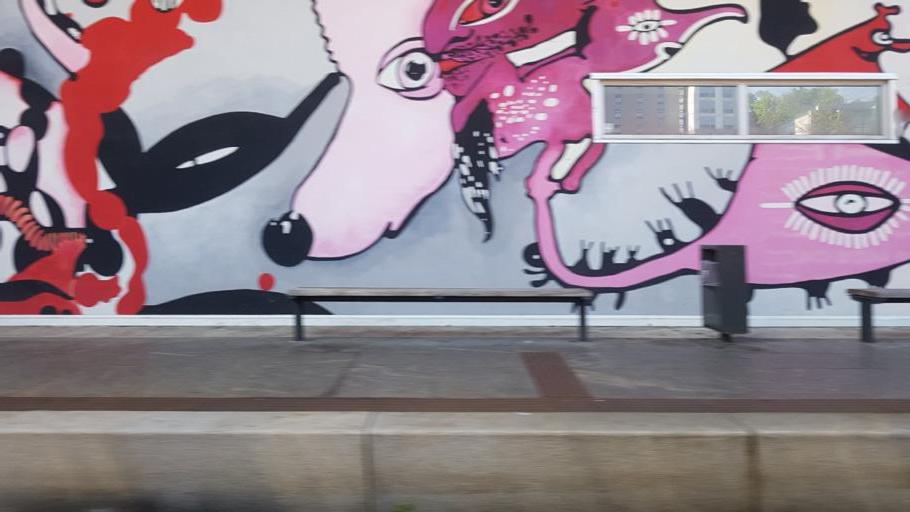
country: NO
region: Hordaland
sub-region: Bergen
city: Bergen
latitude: 60.3458
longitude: 5.3527
